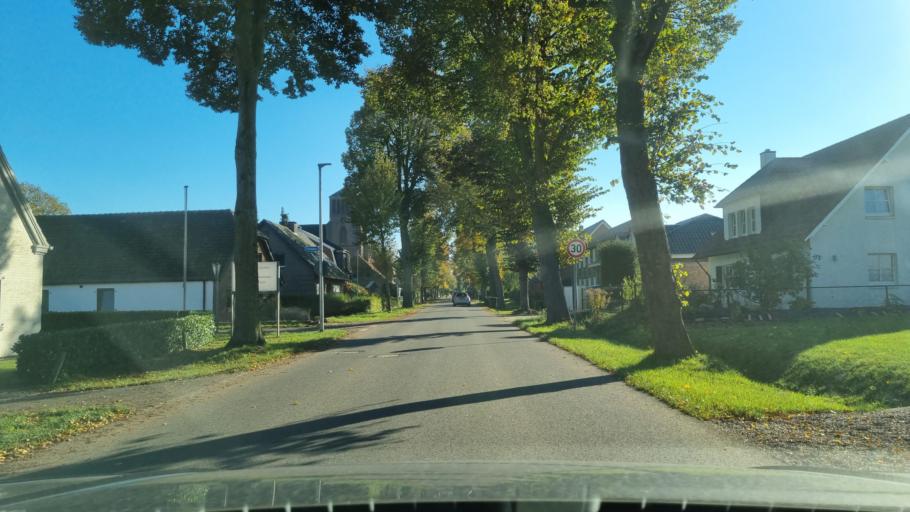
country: DE
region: North Rhine-Westphalia
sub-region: Regierungsbezirk Dusseldorf
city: Kranenburg
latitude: 51.7719
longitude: 6.0229
